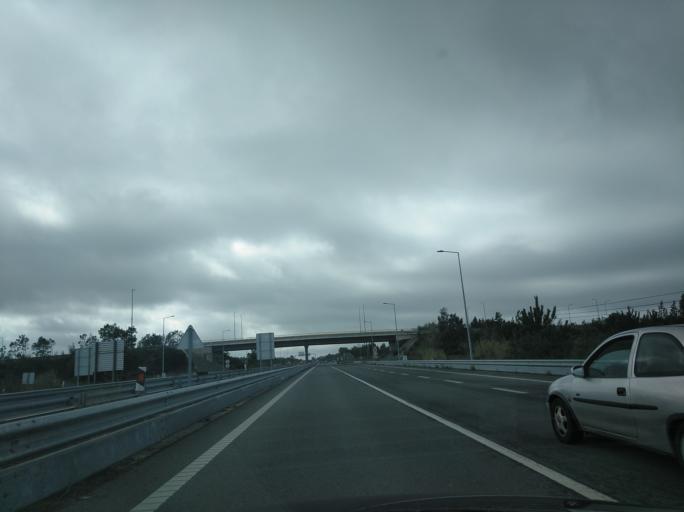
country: PT
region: Setubal
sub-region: Santiago do Cacem
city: Santo Andre
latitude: 38.0398
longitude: -8.7997
